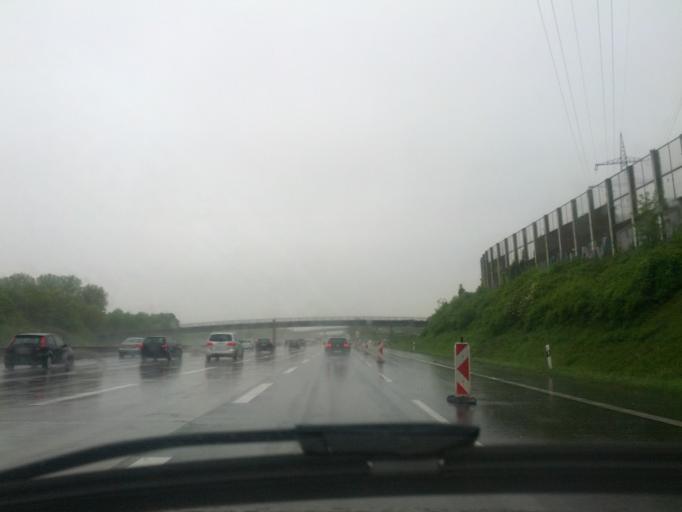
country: DE
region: North Rhine-Westphalia
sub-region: Regierungsbezirk Koln
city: Merheim
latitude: 50.9464
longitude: 7.0393
